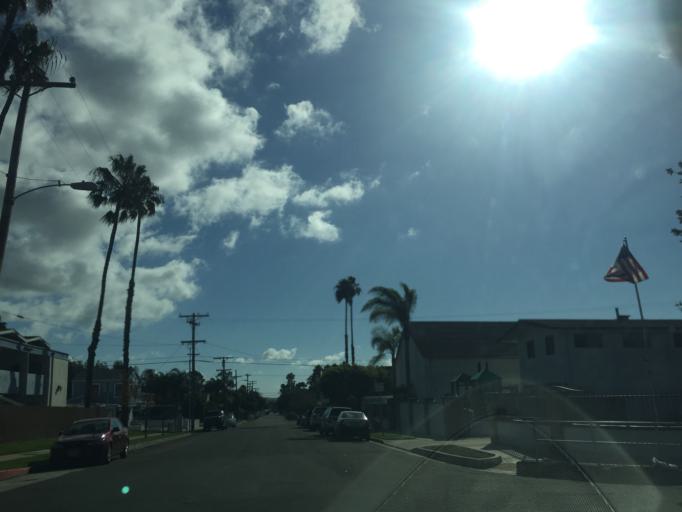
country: US
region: California
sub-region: San Diego County
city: La Jolla
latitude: 32.7952
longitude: -117.2434
